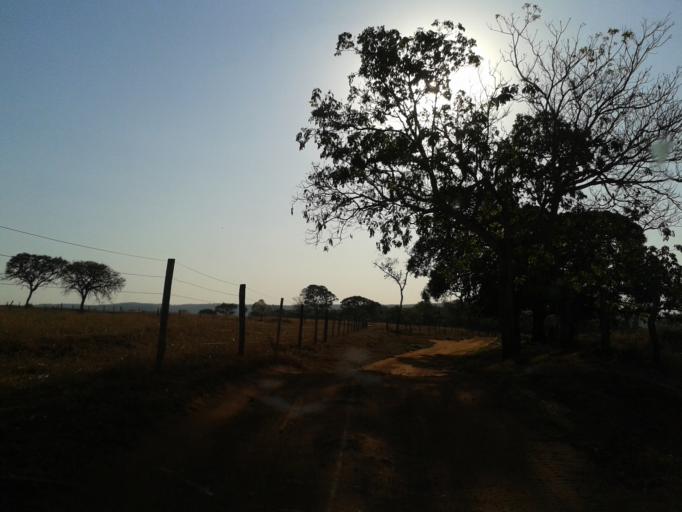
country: BR
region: Minas Gerais
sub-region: Ituiutaba
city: Ituiutaba
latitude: -19.2452
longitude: -49.5885
